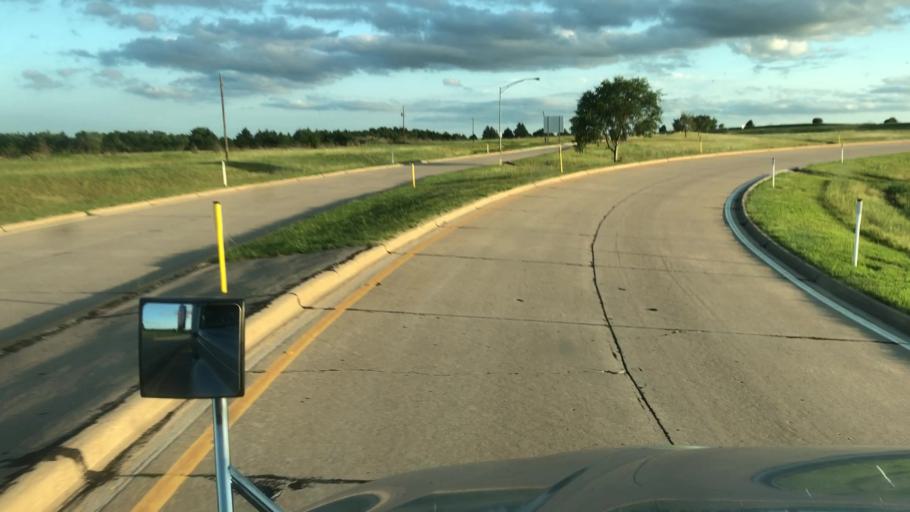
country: US
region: Oklahoma
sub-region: Pawnee County
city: Pawnee
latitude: 36.2967
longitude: -96.9841
